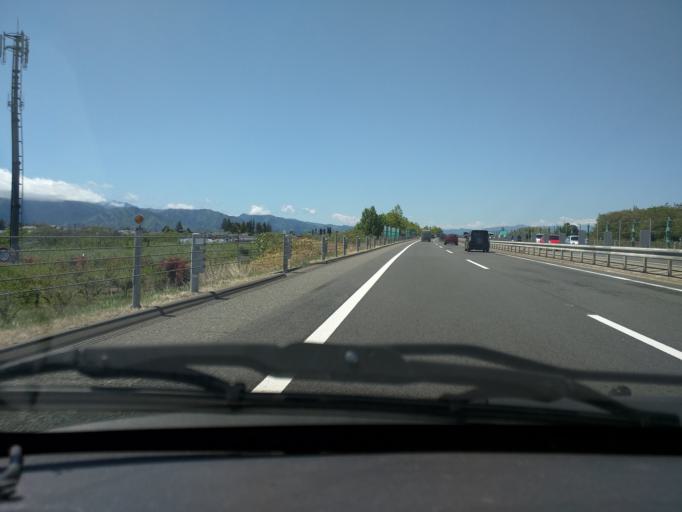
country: JP
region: Nagano
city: Suzaka
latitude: 36.7068
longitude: 138.3059
